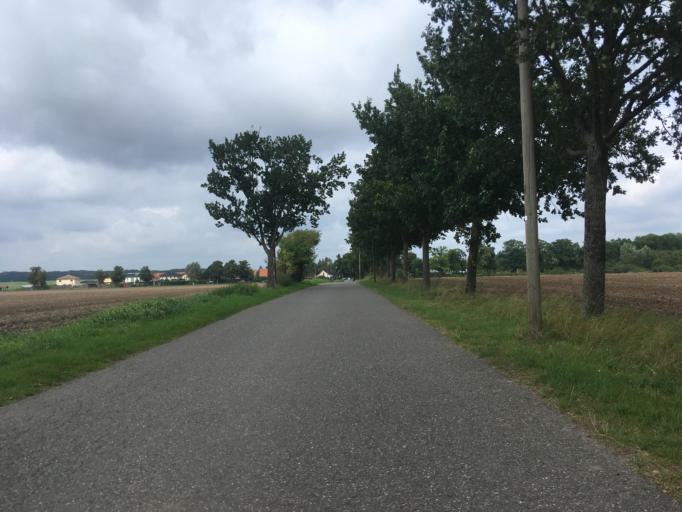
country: DE
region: Brandenburg
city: Glienicke
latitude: 52.6466
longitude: 13.3388
